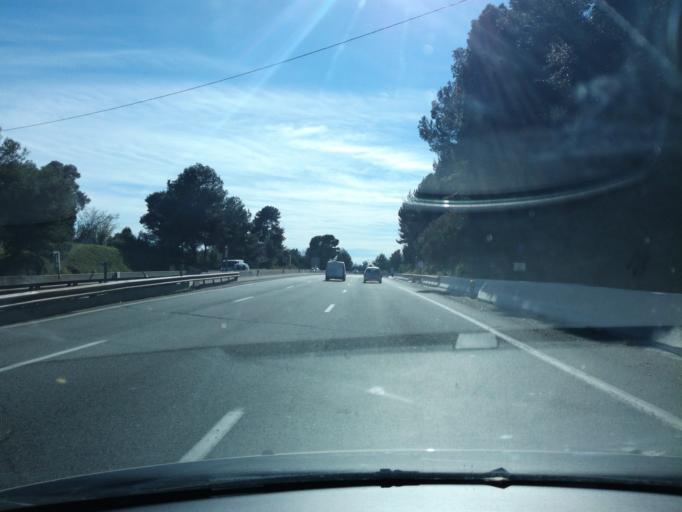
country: FR
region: Provence-Alpes-Cote d'Azur
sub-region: Departement des Alpes-Maritimes
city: Saint-Andre-de-la-Roche
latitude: 43.7309
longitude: 7.2671
